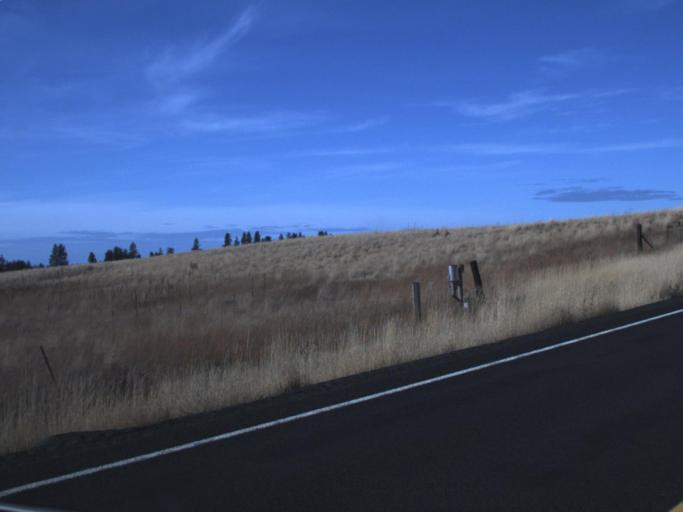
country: US
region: Washington
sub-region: Lincoln County
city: Davenport
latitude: 47.7489
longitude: -118.1722
